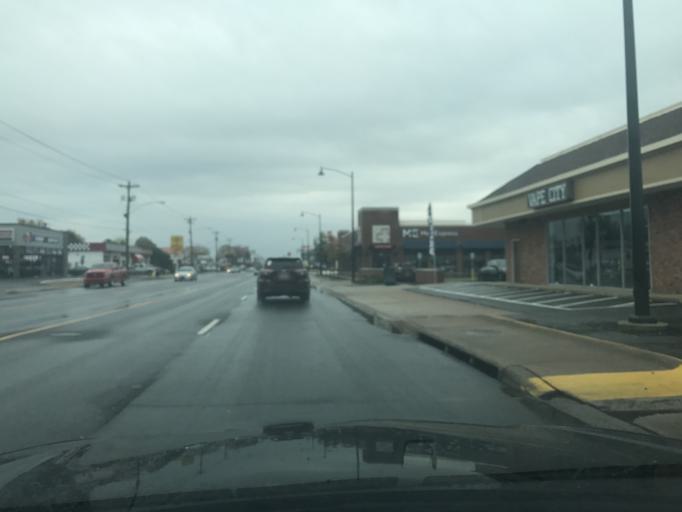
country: US
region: Arkansas
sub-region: Faulkner County
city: Conway
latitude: 35.0917
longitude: -92.4355
